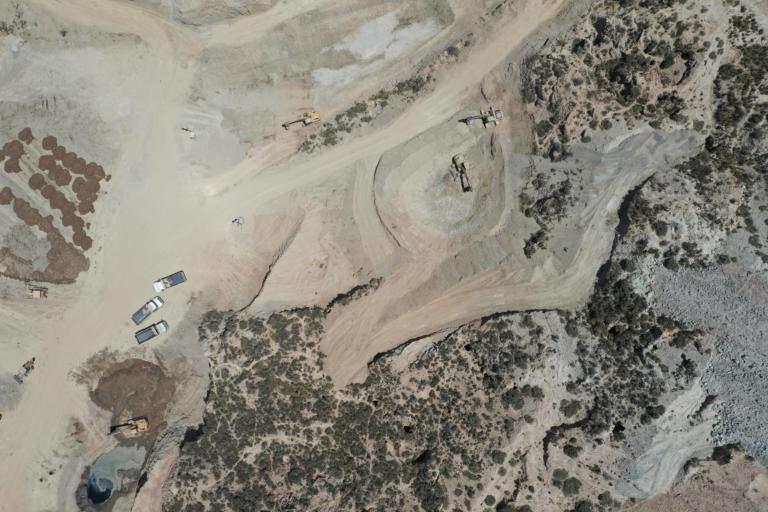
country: BO
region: La Paz
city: La Paz
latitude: -16.5563
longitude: -68.1299
